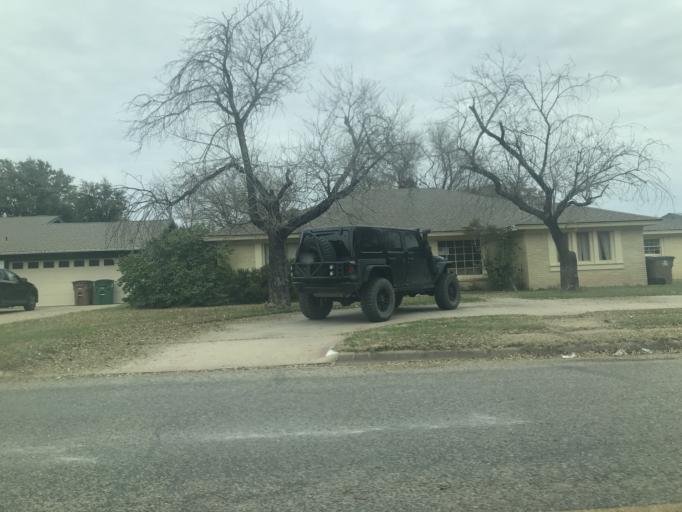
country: US
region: Texas
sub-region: Tom Green County
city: San Angelo
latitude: 31.4233
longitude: -100.4744
